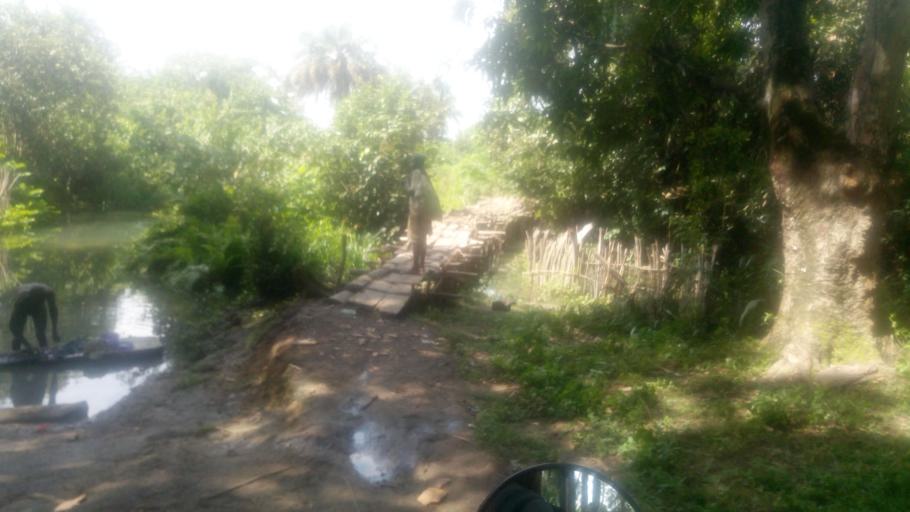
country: SL
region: Northern Province
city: Magburaka
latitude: 8.6641
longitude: -12.0696
